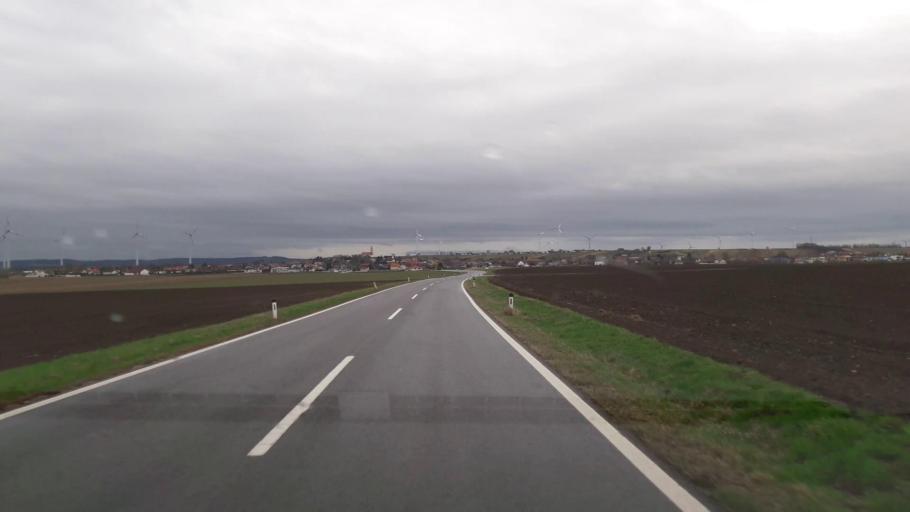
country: AT
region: Lower Austria
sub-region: Politischer Bezirk Bruck an der Leitha
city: Scharndorf
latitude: 48.0799
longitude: 16.7950
